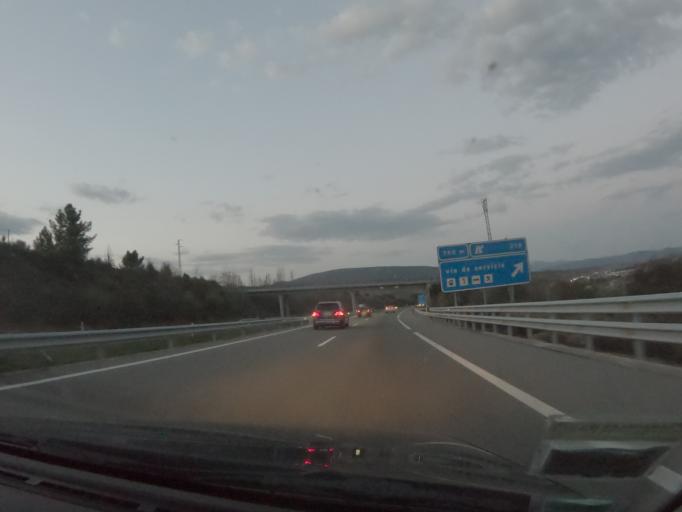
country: ES
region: Castille and Leon
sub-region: Provincia de Leon
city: Congosto
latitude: 42.5835
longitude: -6.5284
